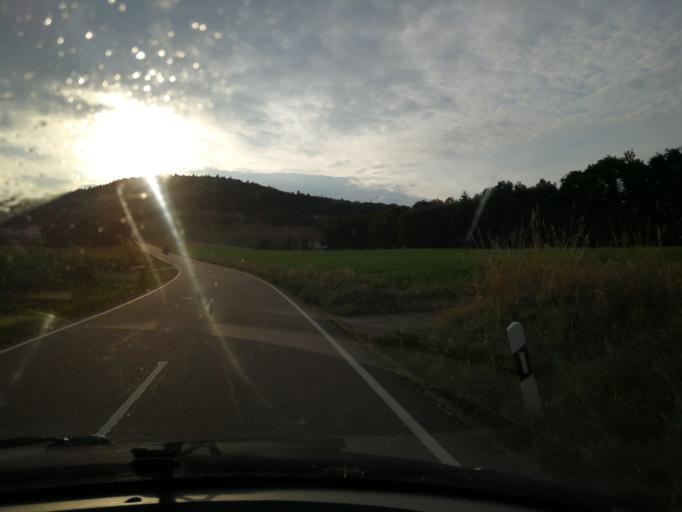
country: DE
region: Bavaria
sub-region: Lower Bavaria
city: Stallwang
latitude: 49.0442
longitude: 12.6216
